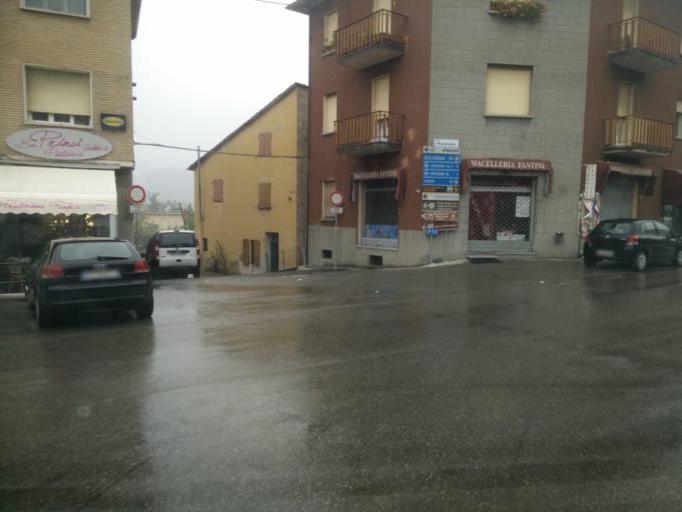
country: IT
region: Emilia-Romagna
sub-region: Provincia di Bologna
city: Grizzana
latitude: 44.2777
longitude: 11.2006
